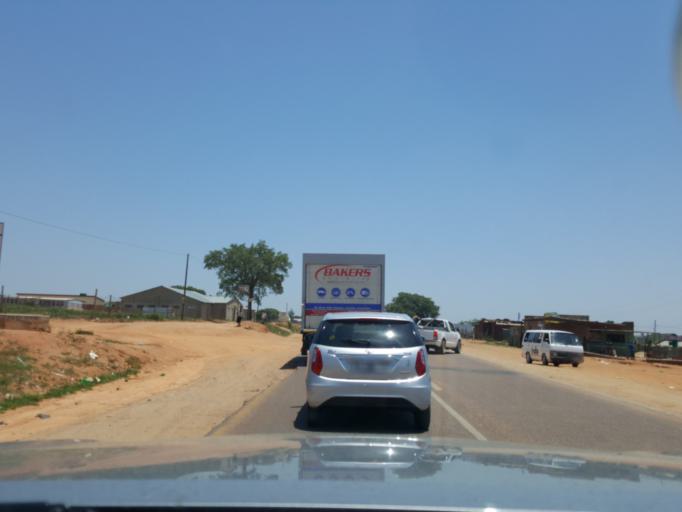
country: ZA
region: Limpopo
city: Thulamahashi
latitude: -24.6190
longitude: 31.0394
